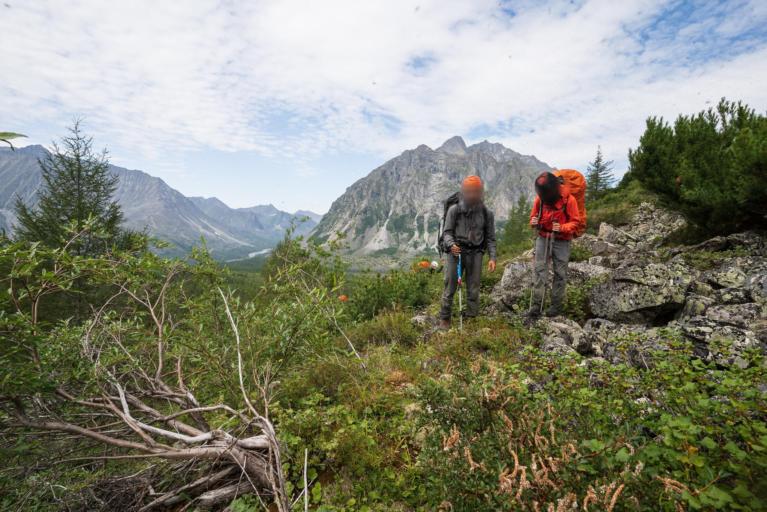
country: RU
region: Transbaikal Territory
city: Chara
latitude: 56.8701
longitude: 117.3186
